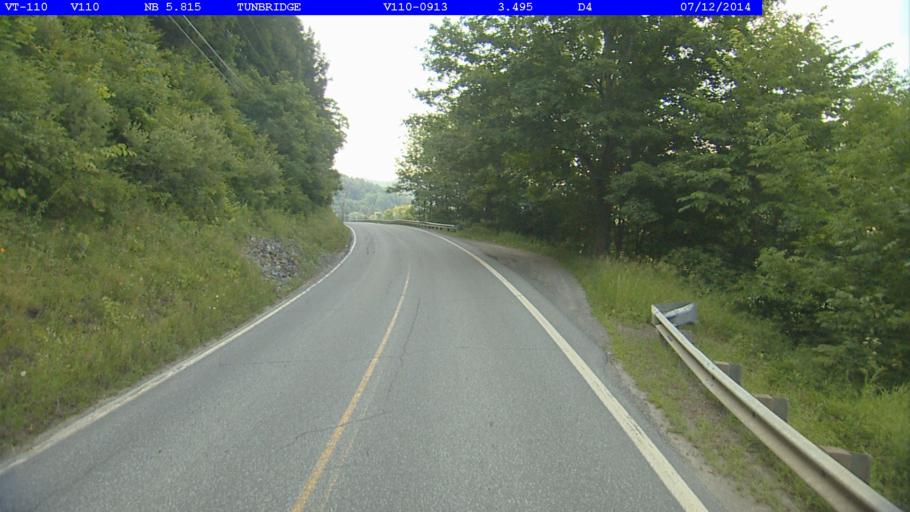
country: US
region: Vermont
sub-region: Orange County
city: Chelsea
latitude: 43.8956
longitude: -72.4851
